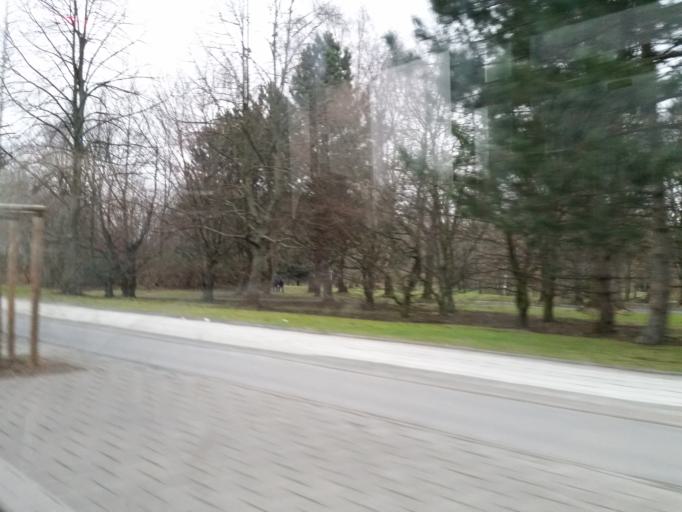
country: DE
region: Lower Saxony
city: Braunschweig
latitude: 52.2519
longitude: 10.5191
